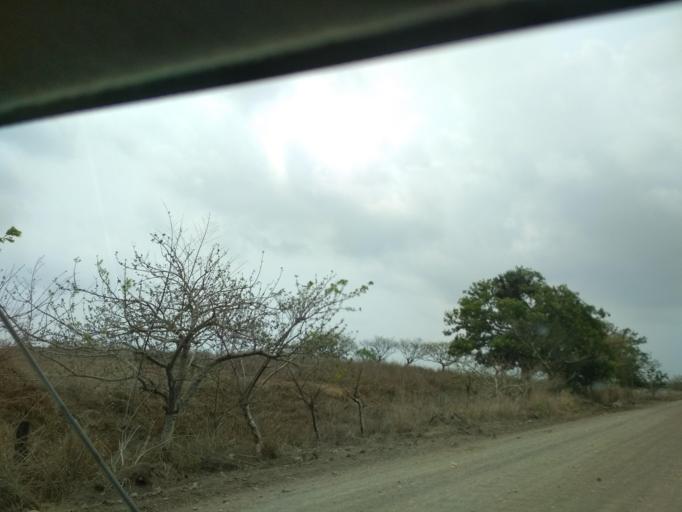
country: MX
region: Veracruz
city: Paso del Toro
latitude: 19.0162
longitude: -96.1346
